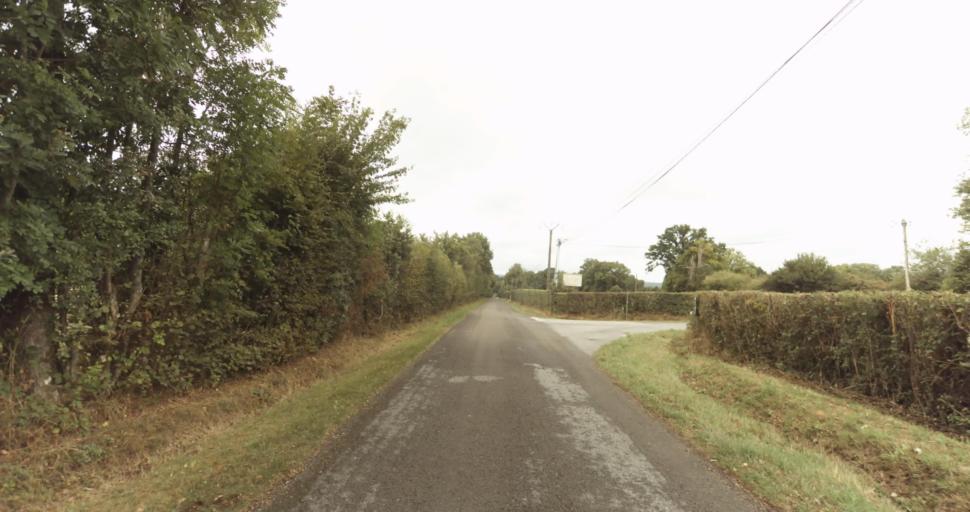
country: FR
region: Lower Normandy
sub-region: Departement de l'Orne
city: Sainte-Gauburge-Sainte-Colombe
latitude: 48.7002
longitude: 0.4519
